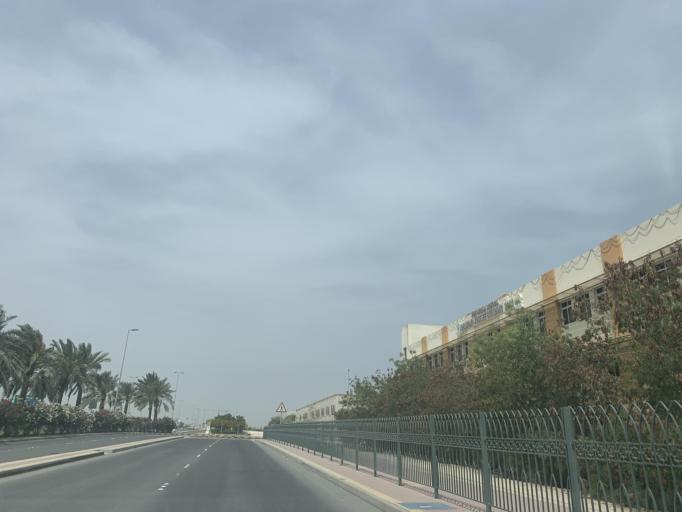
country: BH
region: Northern
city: Madinat `Isa
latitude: 26.1577
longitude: 50.5410
